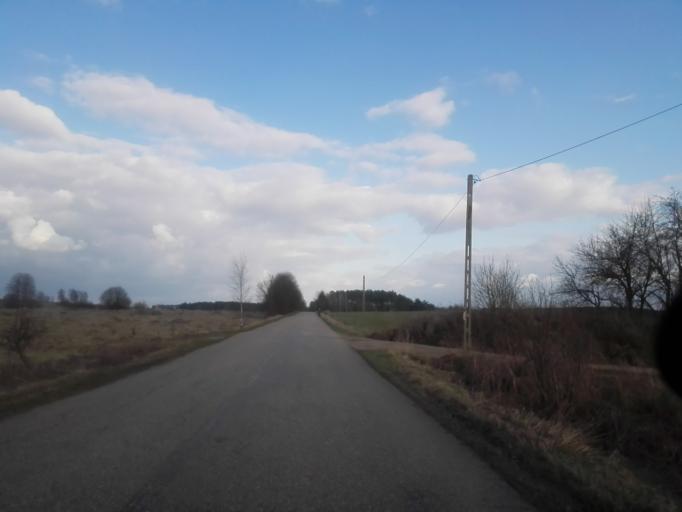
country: PL
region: Podlasie
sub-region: Suwalki
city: Suwalki
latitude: 54.2195
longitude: 22.8461
